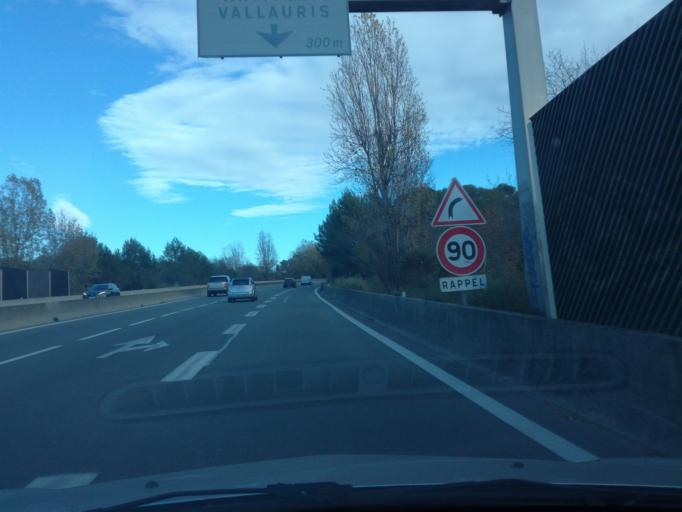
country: FR
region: Provence-Alpes-Cote d'Azur
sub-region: Departement des Alpes-Maritimes
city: Mougins
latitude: 43.6053
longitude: 6.9953
